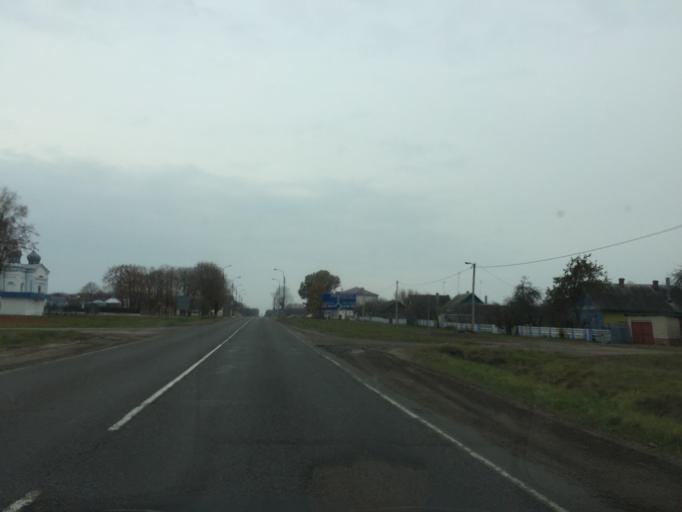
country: BY
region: Gomel
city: Dowsk
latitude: 53.1593
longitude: 30.4641
